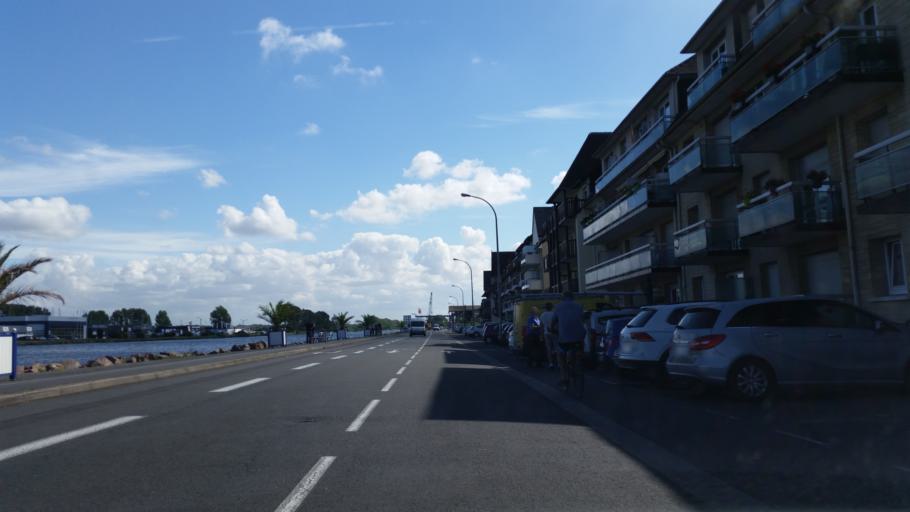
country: FR
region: Lower Normandy
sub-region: Departement du Calvados
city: Ouistreham
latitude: 49.2777
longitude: -0.2505
